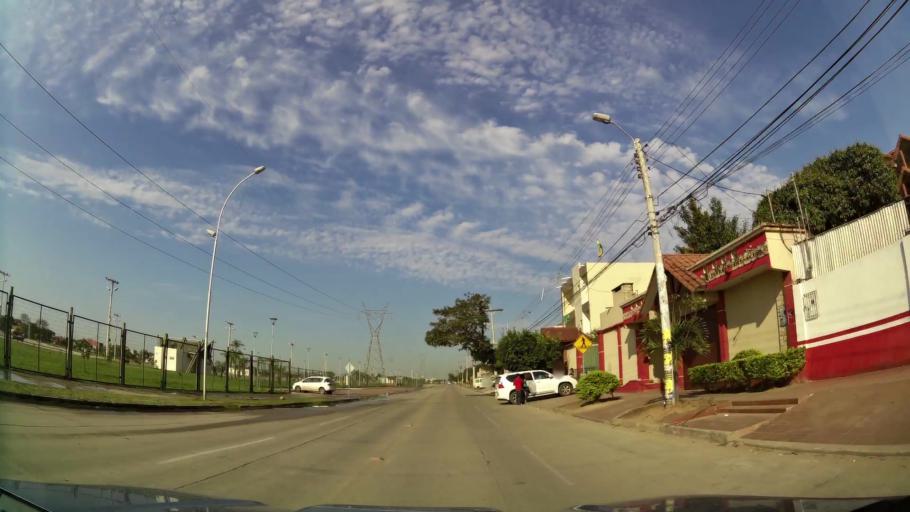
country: BO
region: Santa Cruz
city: Santa Cruz de la Sierra
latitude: -17.7428
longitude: -63.1469
